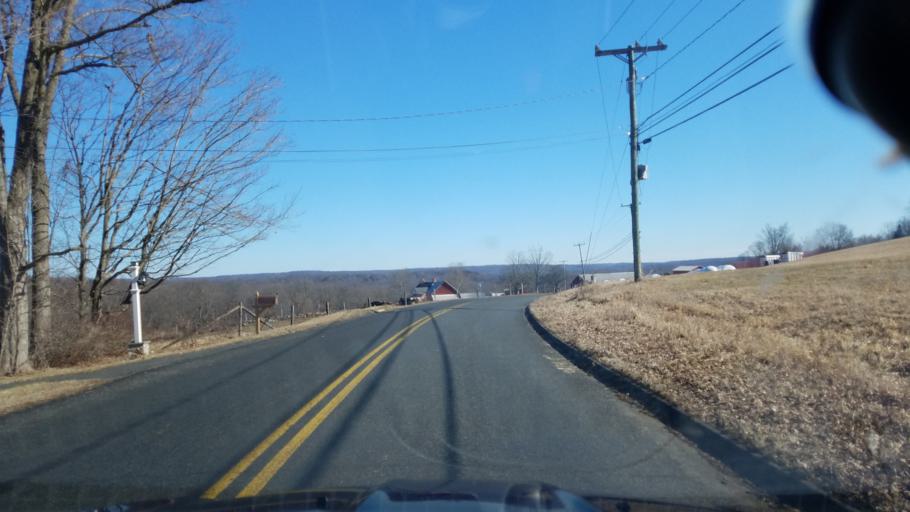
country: US
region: Connecticut
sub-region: New Haven County
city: Heritage Village
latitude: 41.4878
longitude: -73.2776
